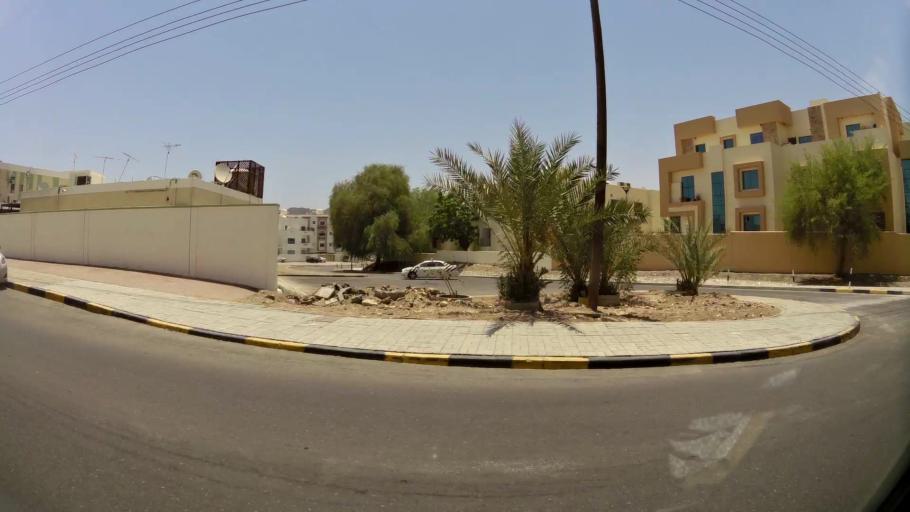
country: OM
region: Muhafazat Masqat
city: Muscat
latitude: 23.6053
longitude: 58.5390
